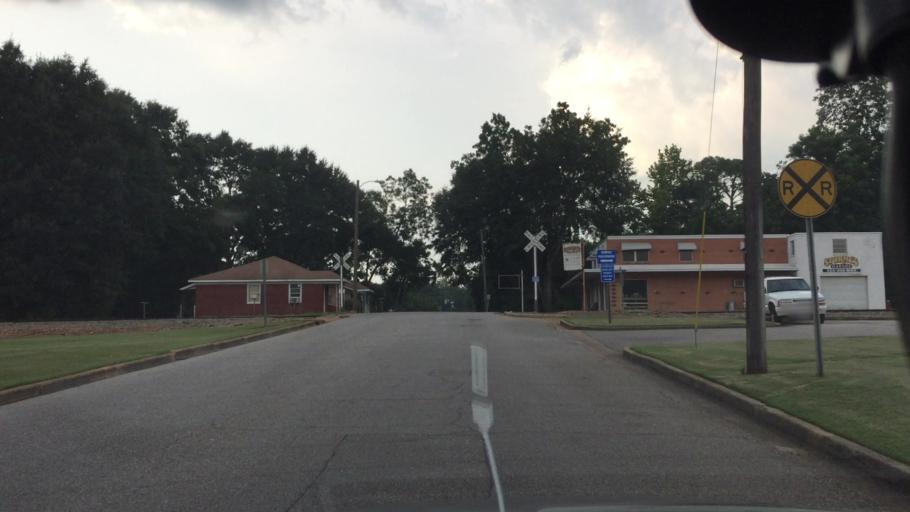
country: US
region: Alabama
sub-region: Coffee County
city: Enterprise
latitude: 31.3102
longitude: -85.8501
